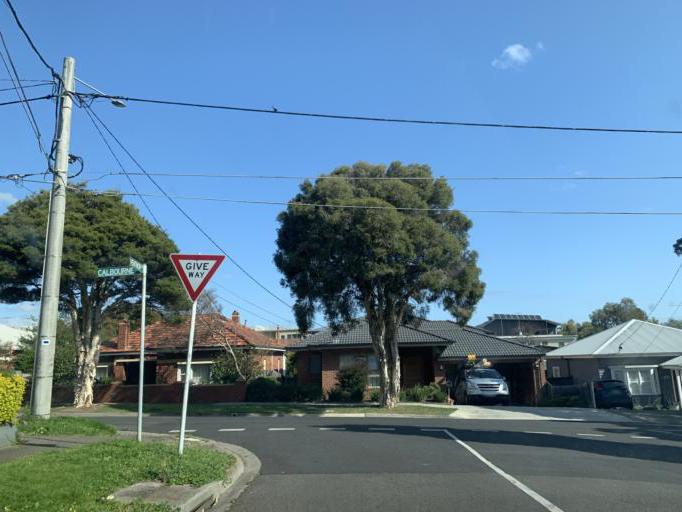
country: AU
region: Victoria
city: Thornbury
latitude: -37.7492
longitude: 144.9841
